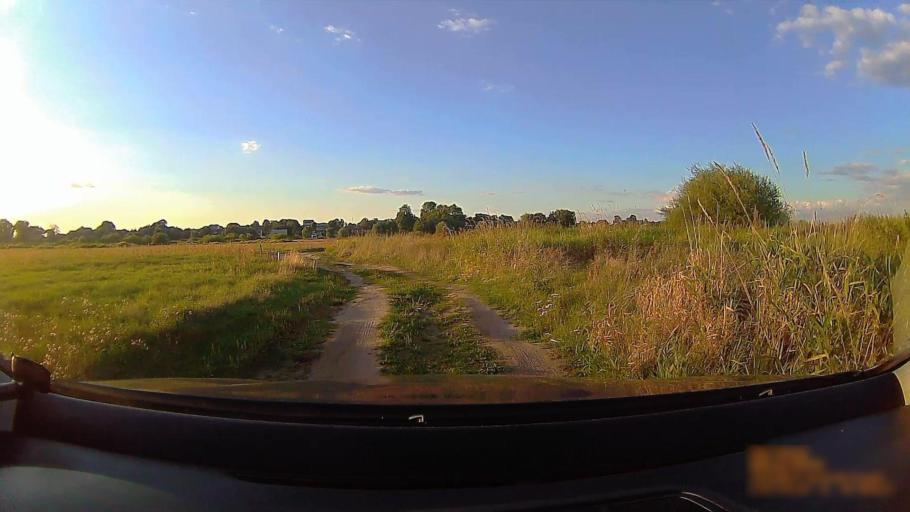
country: PL
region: Greater Poland Voivodeship
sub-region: Konin
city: Konin
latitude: 52.2182
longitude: 18.3148
